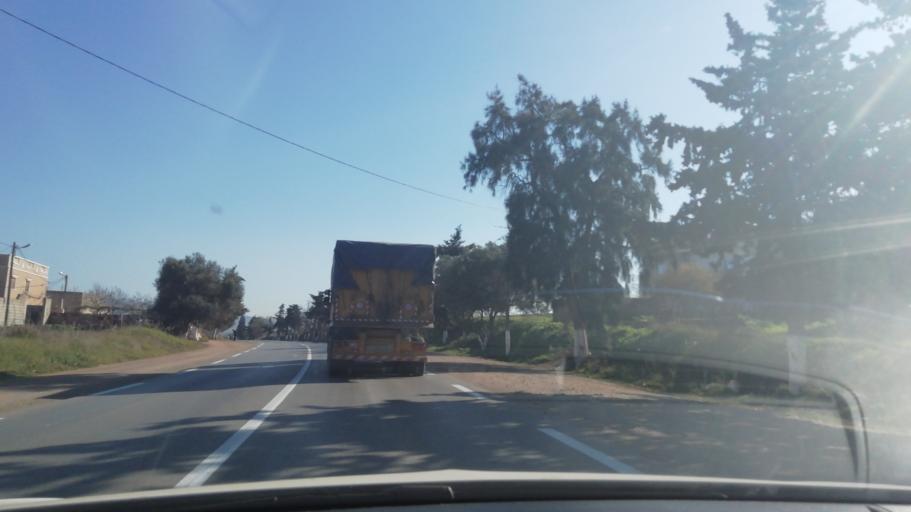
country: DZ
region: Tlemcen
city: Nedroma
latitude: 35.0844
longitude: -1.7986
